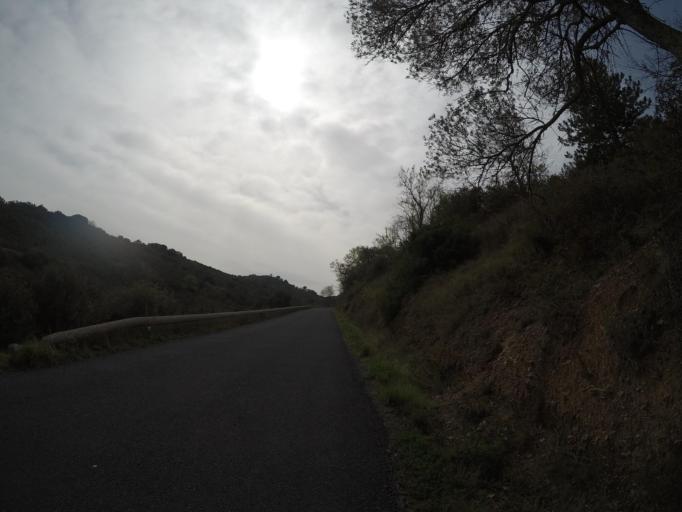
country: FR
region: Languedoc-Roussillon
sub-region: Departement des Pyrenees-Orientales
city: Estagel
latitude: 42.7481
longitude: 2.7241
